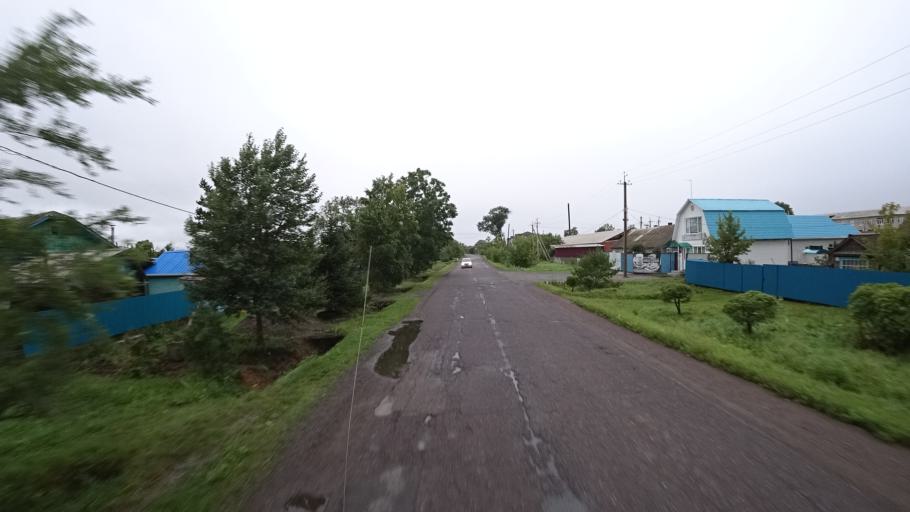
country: RU
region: Primorskiy
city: Chernigovka
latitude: 44.3369
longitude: 132.5768
